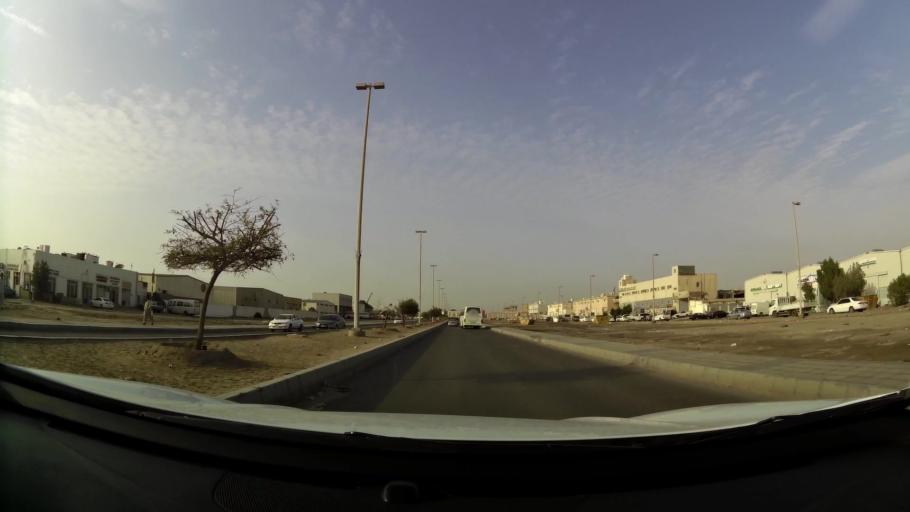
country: AE
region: Abu Dhabi
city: Abu Dhabi
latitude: 24.3513
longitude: 54.5170
